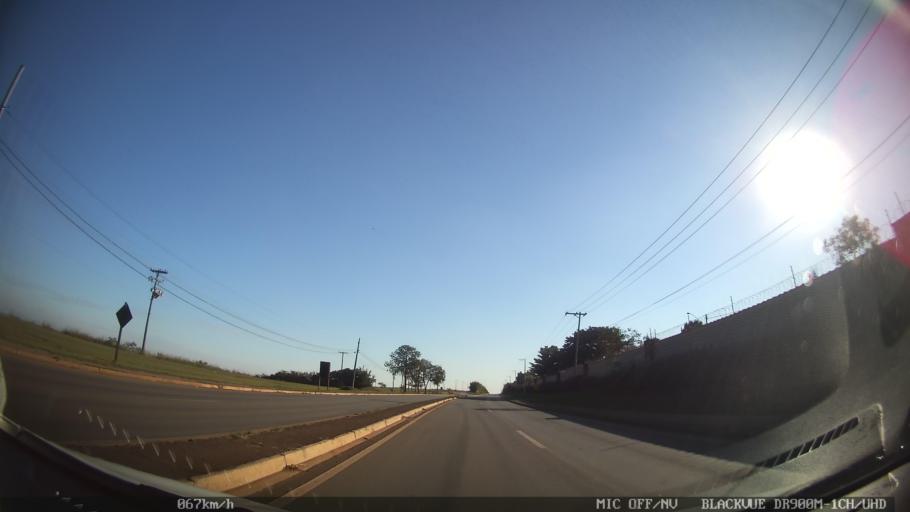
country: BR
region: Sao Paulo
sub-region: Nova Odessa
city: Nova Odessa
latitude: -22.7665
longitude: -47.2643
